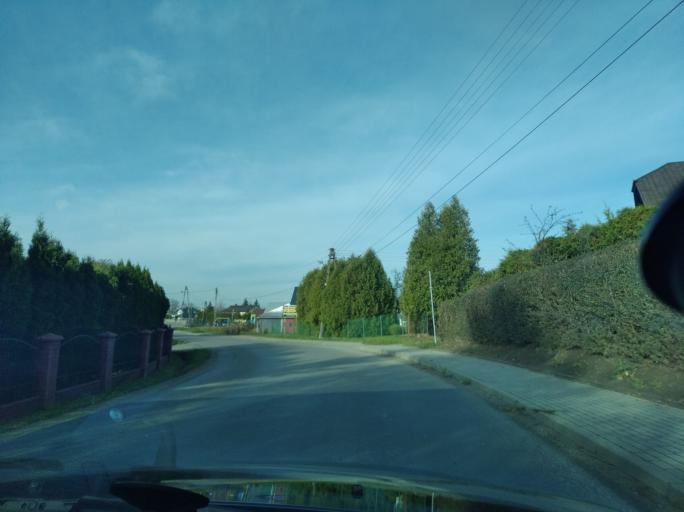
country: PL
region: Subcarpathian Voivodeship
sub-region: Powiat rzeszowski
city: Krasne
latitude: 50.0331
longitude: 22.0949
